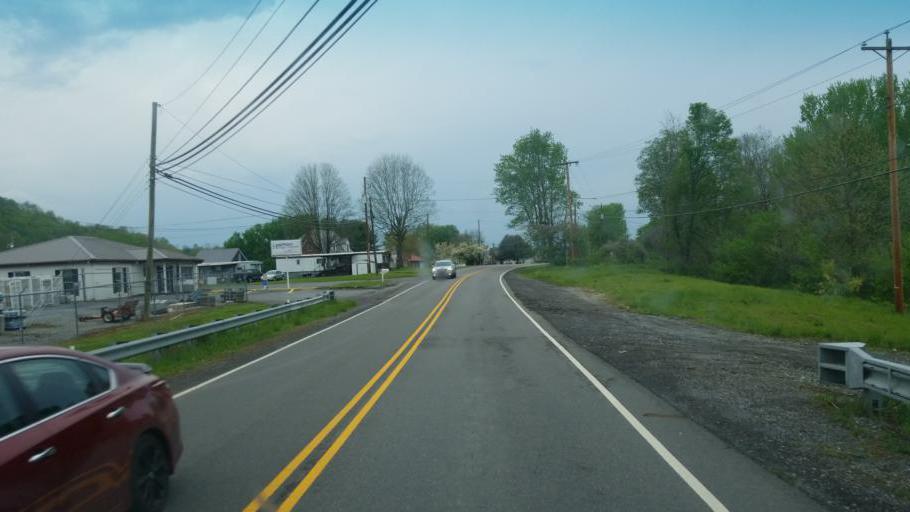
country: US
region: Virginia
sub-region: Smyth County
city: Adwolf
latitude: 36.8076
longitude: -81.6225
